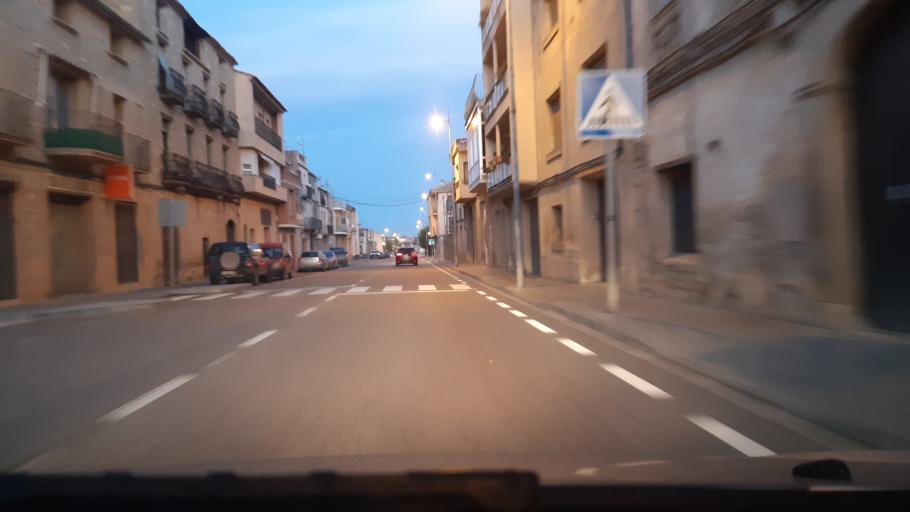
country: ES
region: Aragon
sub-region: Provincia de Teruel
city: Calaceite
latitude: 41.0158
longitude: 0.1899
